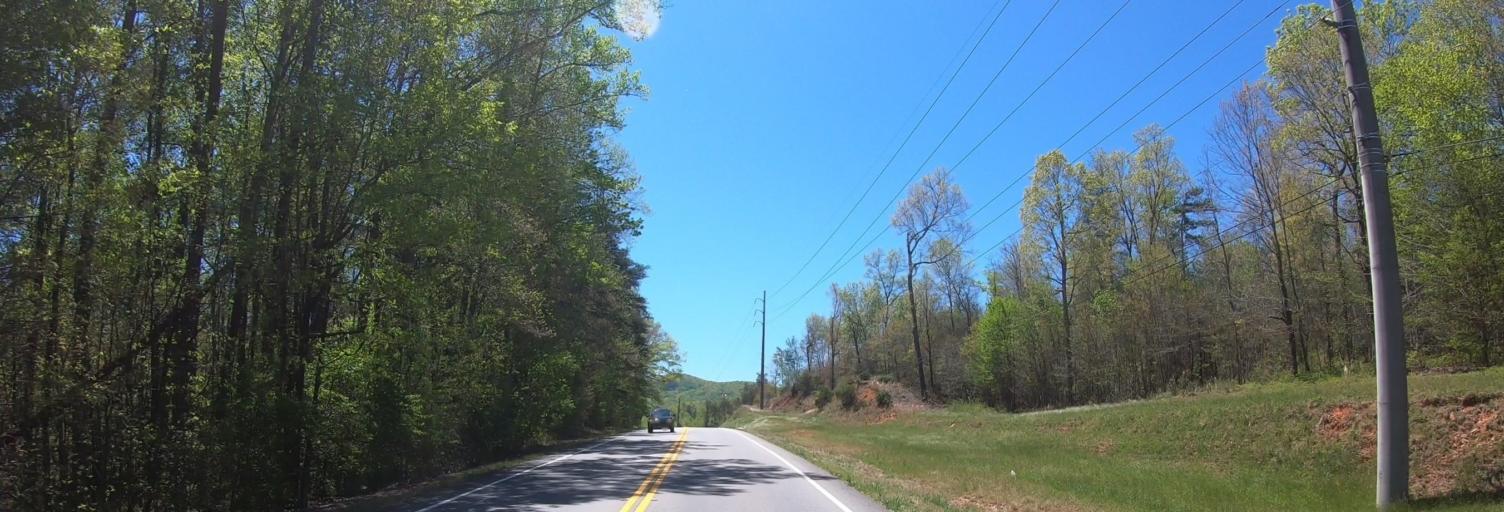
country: US
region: Georgia
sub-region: White County
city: Cleveland
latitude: 34.6796
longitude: -83.7132
